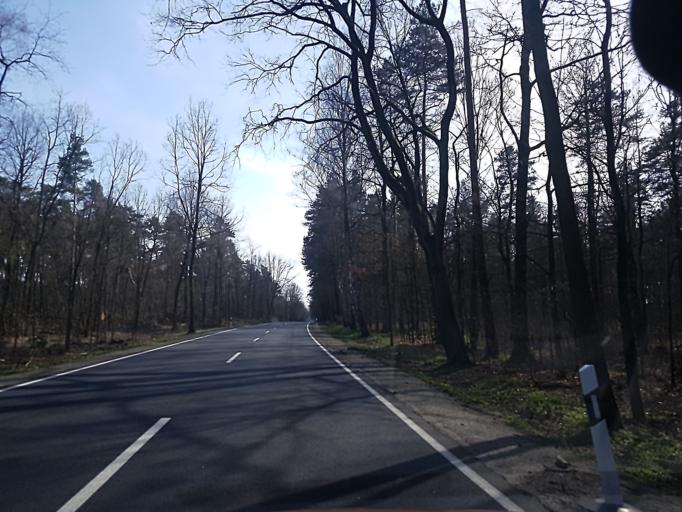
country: DE
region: Brandenburg
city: Bronkow
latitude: 51.6986
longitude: 13.9194
